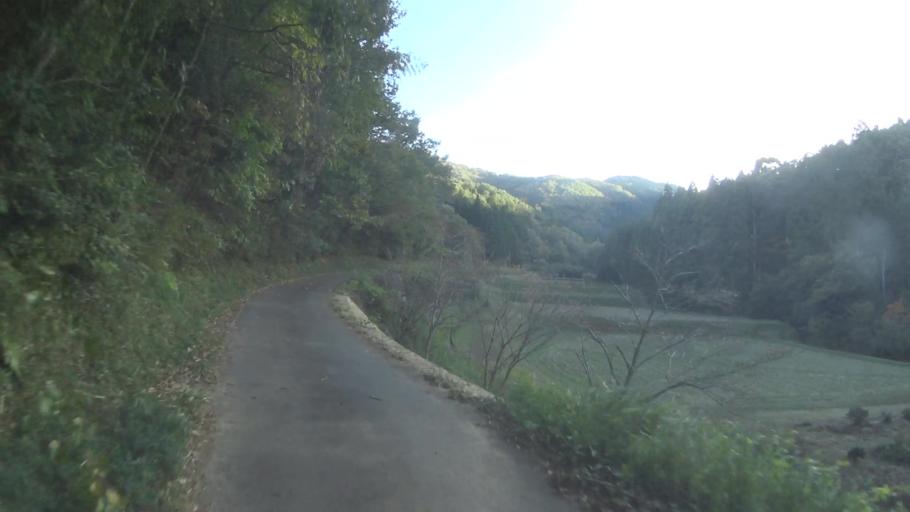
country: JP
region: Kyoto
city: Ayabe
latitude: 35.2762
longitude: 135.2494
